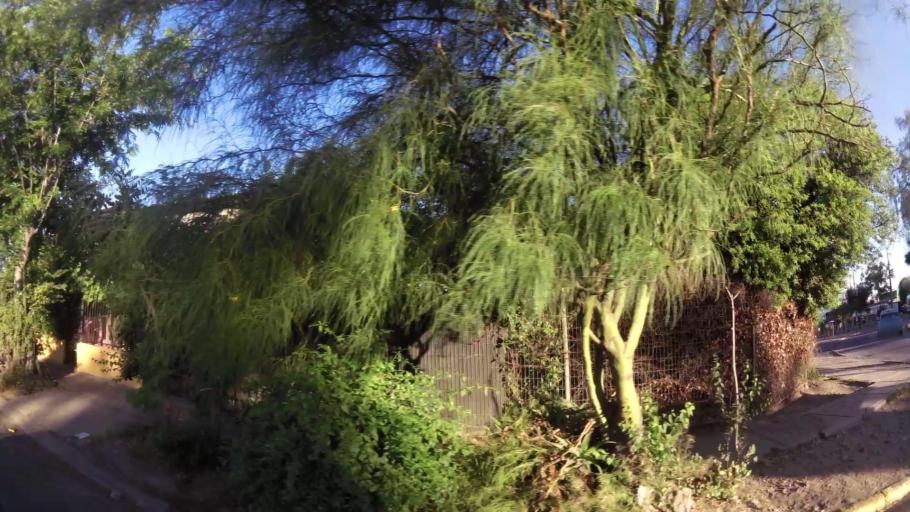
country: CL
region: Santiago Metropolitan
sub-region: Provincia de Maipo
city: San Bernardo
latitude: -33.5859
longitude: -70.6891
